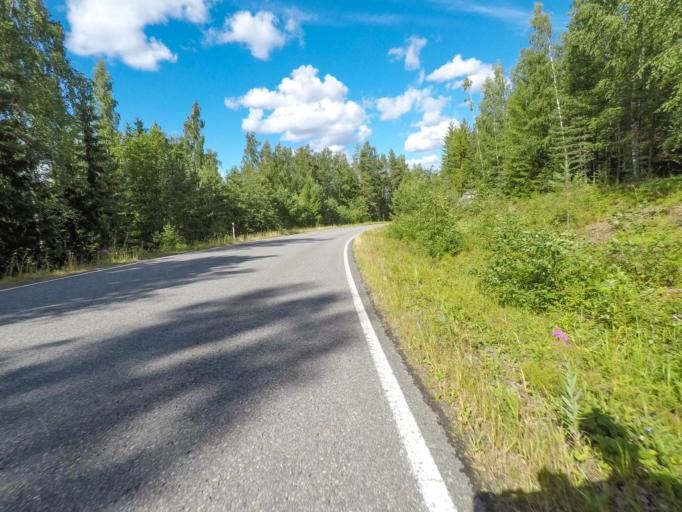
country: FI
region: South Karelia
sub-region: Lappeenranta
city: Joutseno
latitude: 61.0994
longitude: 28.3631
